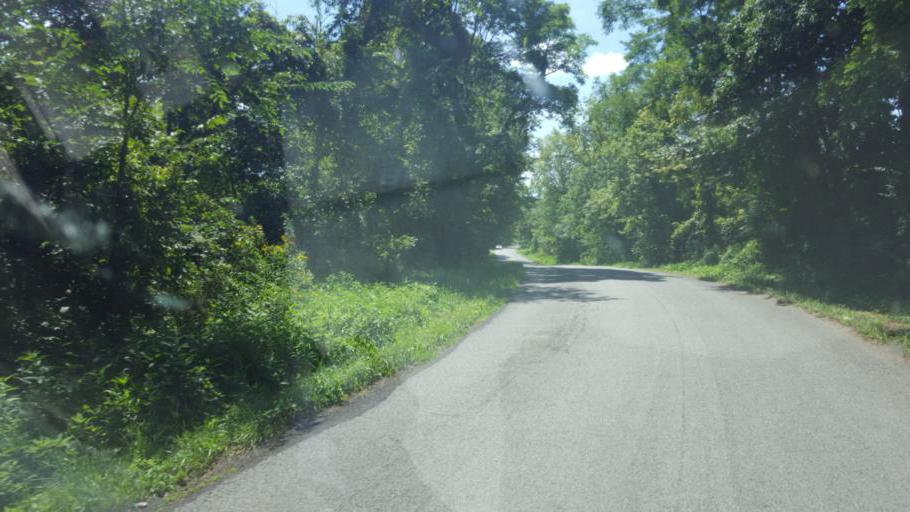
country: US
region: Ohio
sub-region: Knox County
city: Centerburg
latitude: 40.3640
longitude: -82.7919
